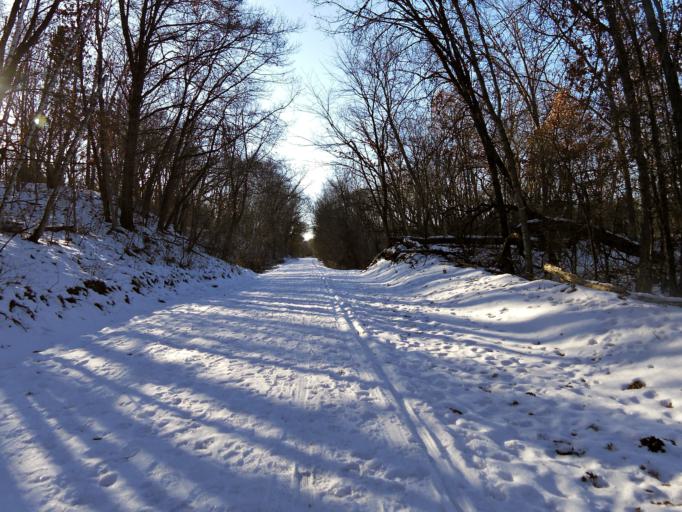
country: US
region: Minnesota
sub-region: Washington County
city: Grant
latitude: 45.0779
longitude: -92.8912
